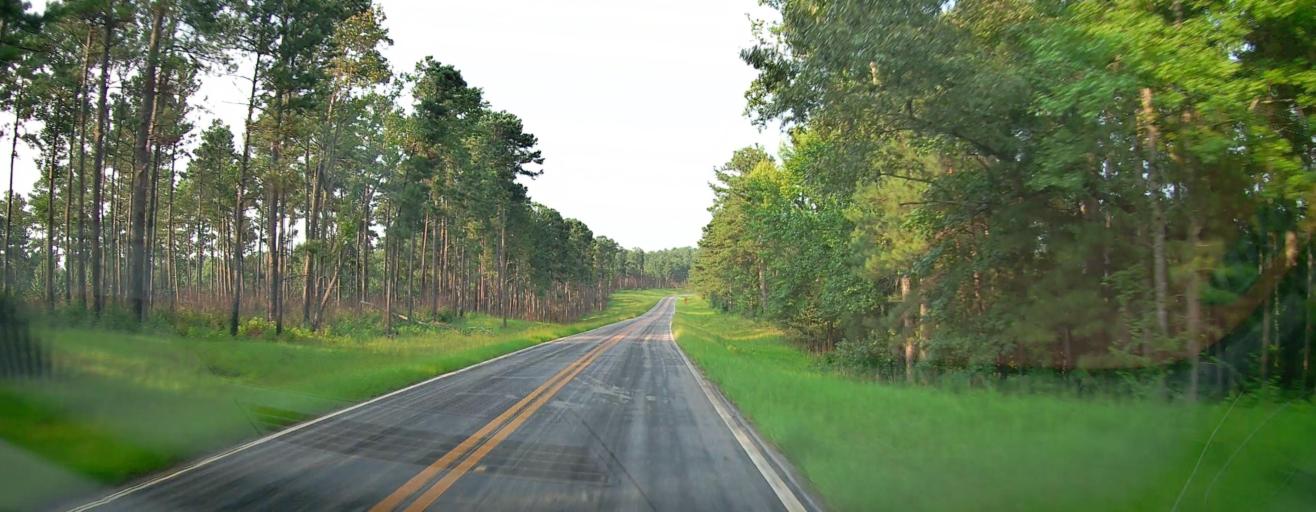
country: US
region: Georgia
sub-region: Jones County
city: Gray
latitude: 33.1110
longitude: -83.6573
